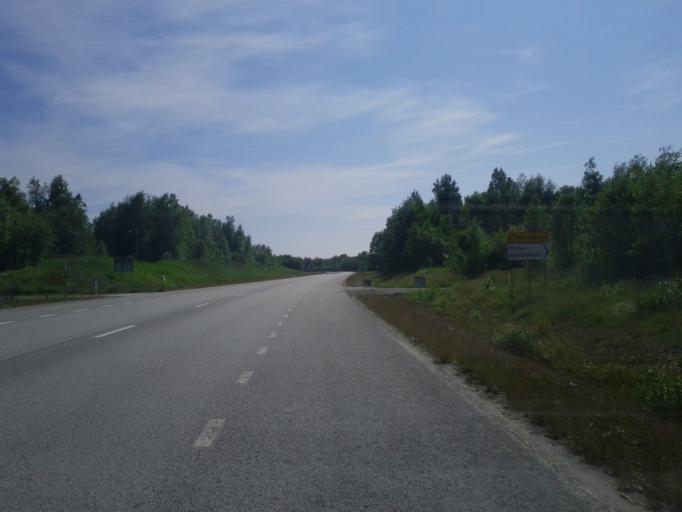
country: SE
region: Vaesterbotten
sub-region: Umea Kommun
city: Umea
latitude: 63.7794
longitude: 20.3024
